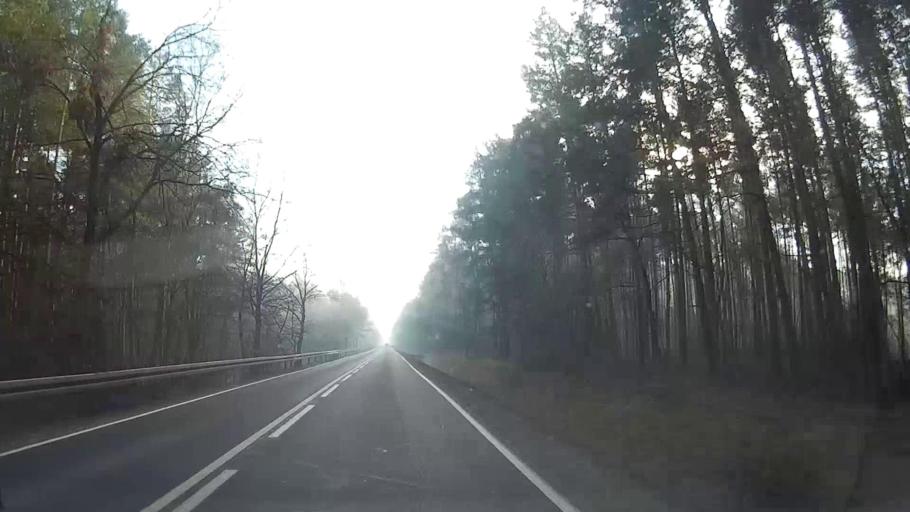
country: PL
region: Lesser Poland Voivodeship
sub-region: Powiat chrzanowski
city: Zarki
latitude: 50.0816
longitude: 19.3694
